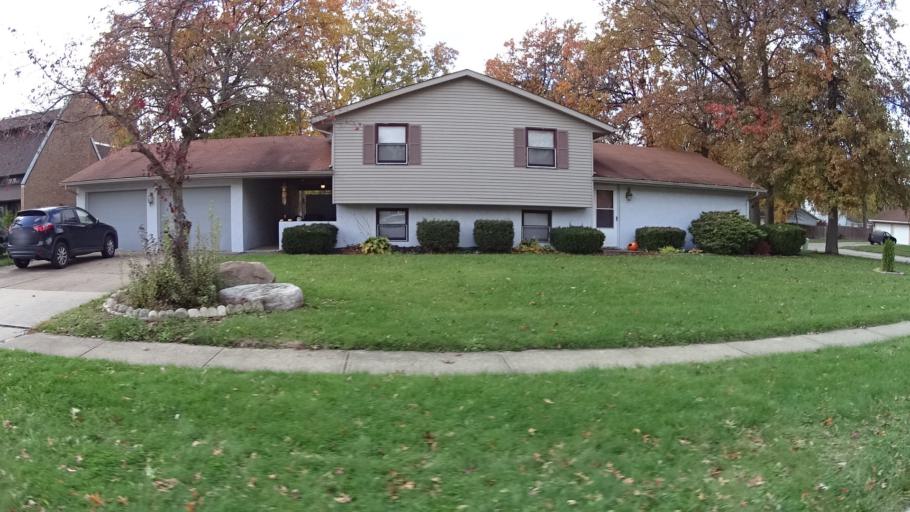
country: US
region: Ohio
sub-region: Lorain County
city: Lorain
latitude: 41.4259
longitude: -82.1899
